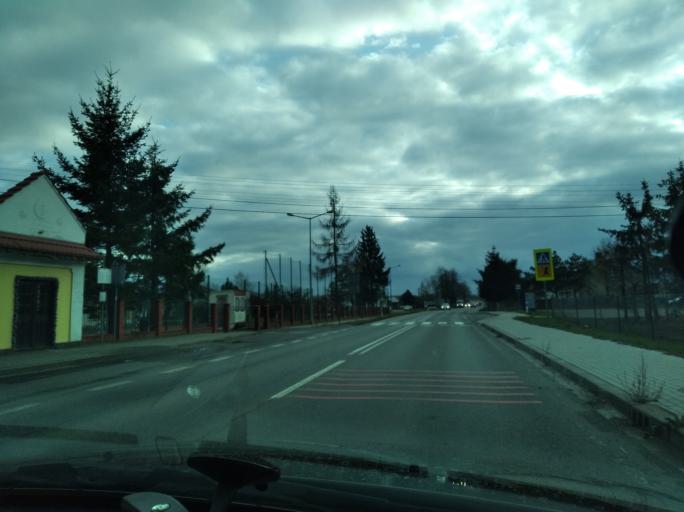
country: PL
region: Subcarpathian Voivodeship
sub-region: Powiat lancucki
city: Rakszawa
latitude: 50.1183
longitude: 22.2324
